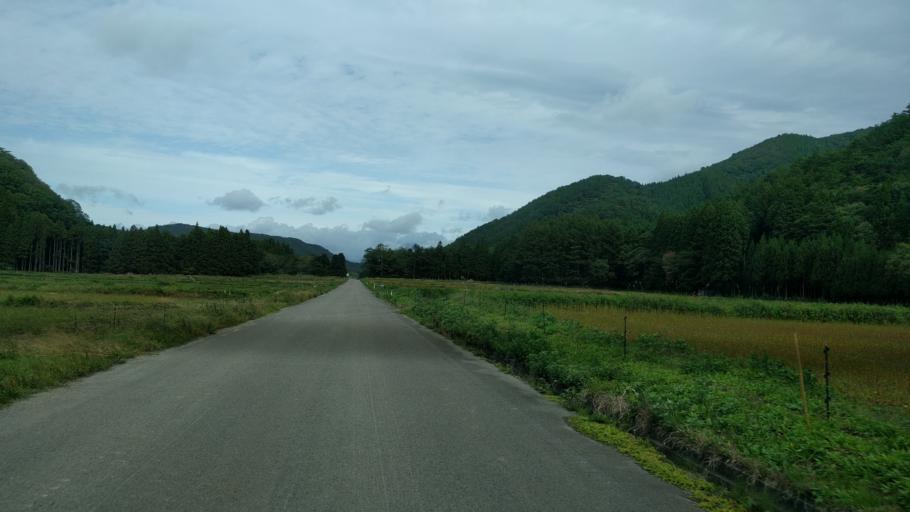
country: JP
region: Fukushima
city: Inawashiro
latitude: 37.3829
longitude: 140.1515
